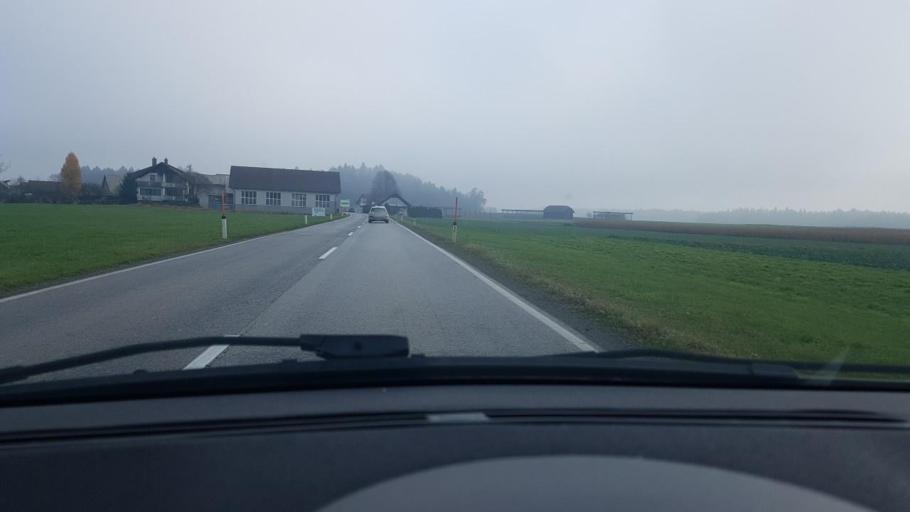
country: SI
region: Vodice
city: Vodice
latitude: 46.2172
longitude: 14.5025
